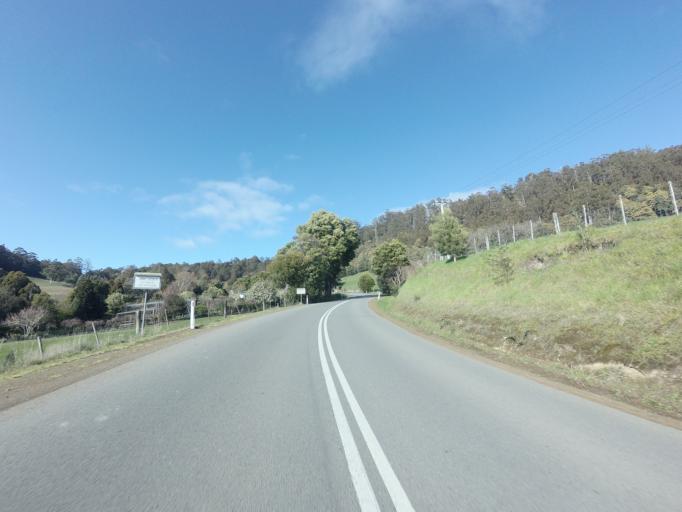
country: AU
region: Tasmania
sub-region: Huon Valley
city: Geeveston
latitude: -43.2444
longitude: 146.9911
